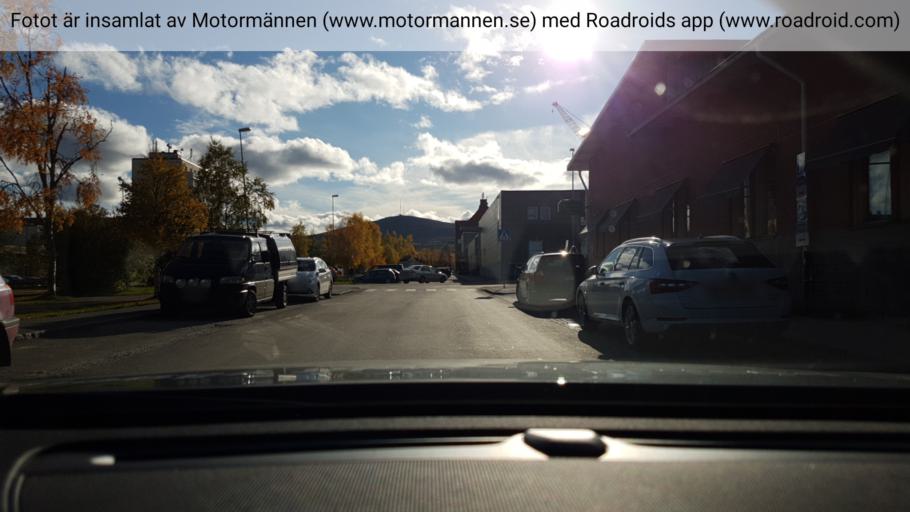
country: SE
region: Norrbotten
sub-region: Gallivare Kommun
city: Gaellivare
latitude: 67.1356
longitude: 20.6640
